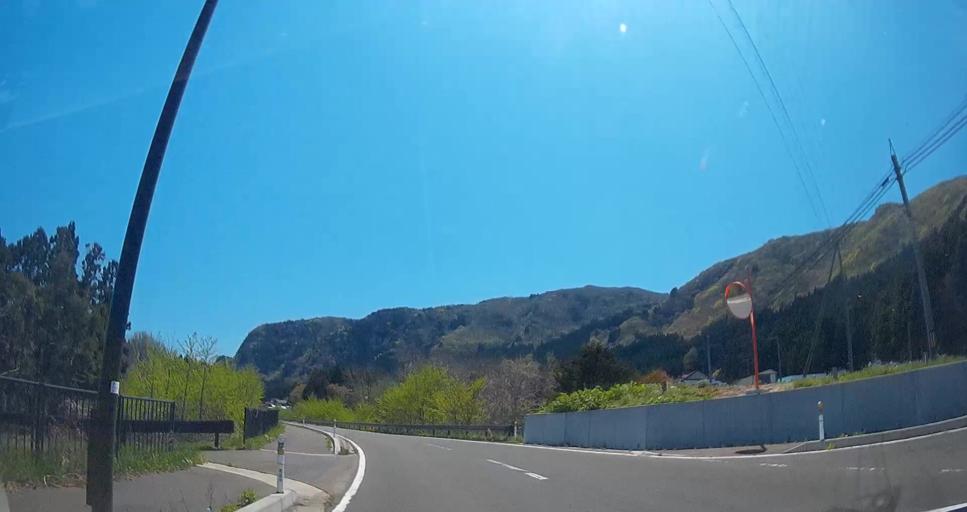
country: JP
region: Aomori
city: Mutsu
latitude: 41.4017
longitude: 141.4469
